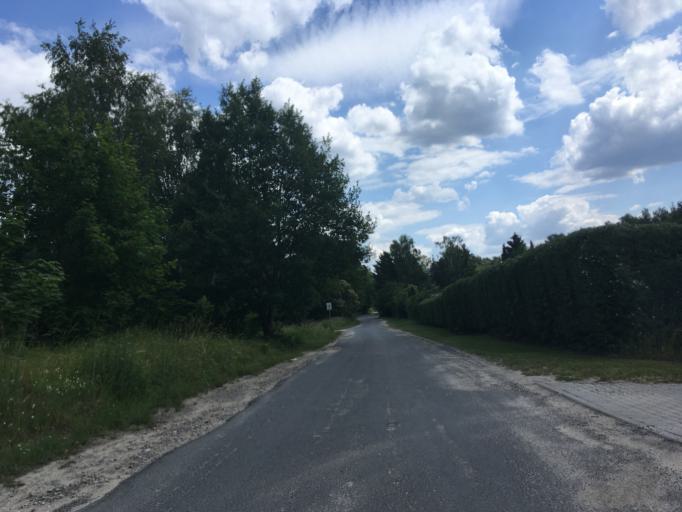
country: DE
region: Brandenburg
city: Rehfelde
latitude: 52.5408
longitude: 13.9091
